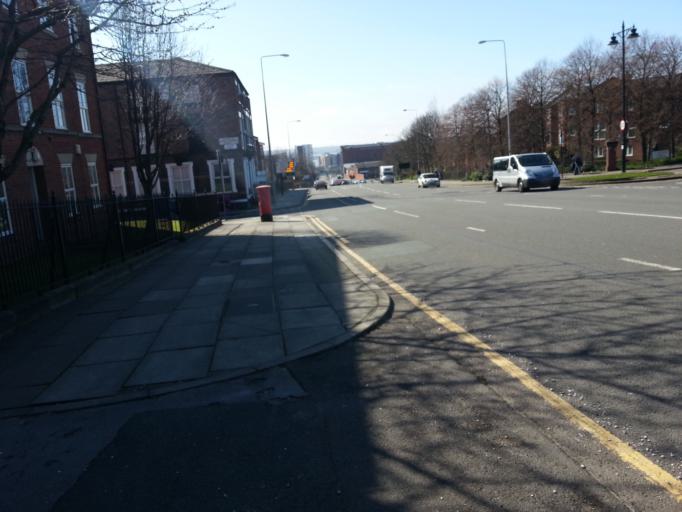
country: GB
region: England
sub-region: Liverpool
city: Liverpool
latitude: 53.3950
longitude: -2.9727
